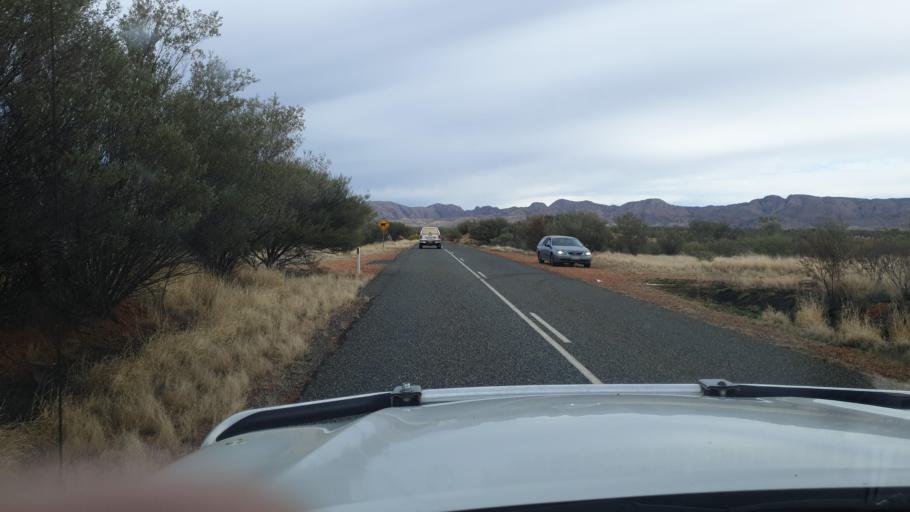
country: AU
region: Northern Territory
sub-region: Alice Springs
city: Alice Springs
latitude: -23.7847
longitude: 133.5126
